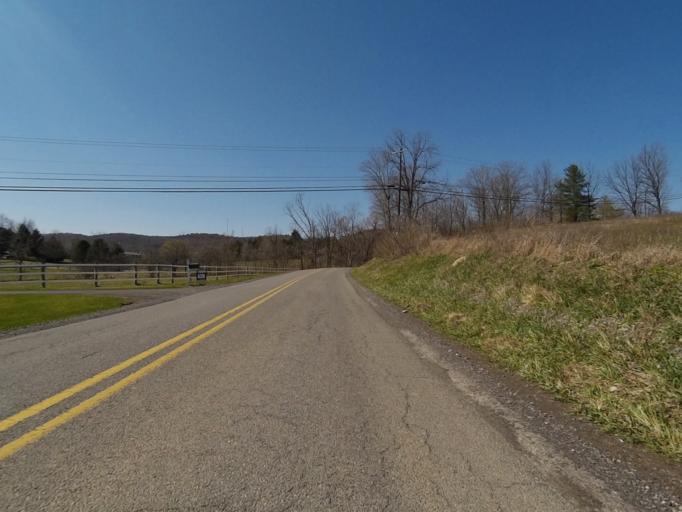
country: US
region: Pennsylvania
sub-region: Centre County
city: Stormstown
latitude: 40.7715
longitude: -78.0402
